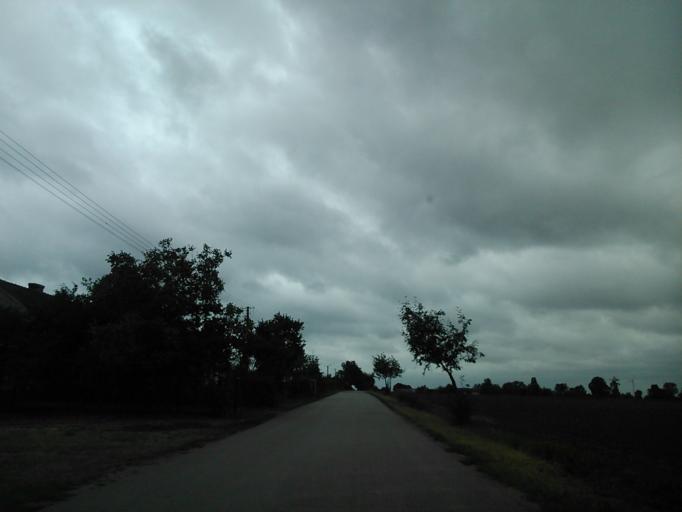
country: PL
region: Kujawsko-Pomorskie
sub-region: Powiat inowroclawski
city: Inowroclaw
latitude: 52.7679
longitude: 18.3348
